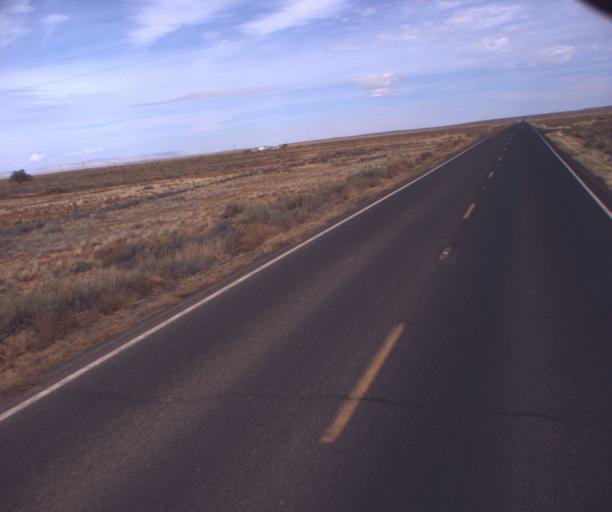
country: US
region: Arizona
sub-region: Apache County
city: Ganado
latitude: 35.8055
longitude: -109.6121
